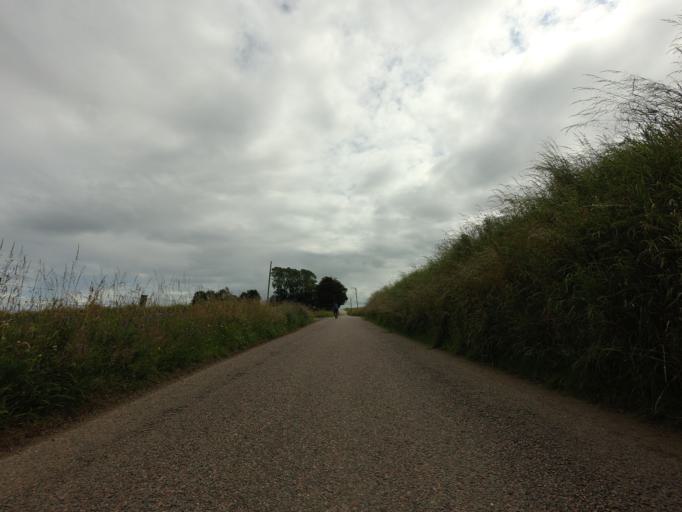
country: GB
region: Scotland
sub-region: Moray
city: Fochabers
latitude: 57.6671
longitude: -3.1507
